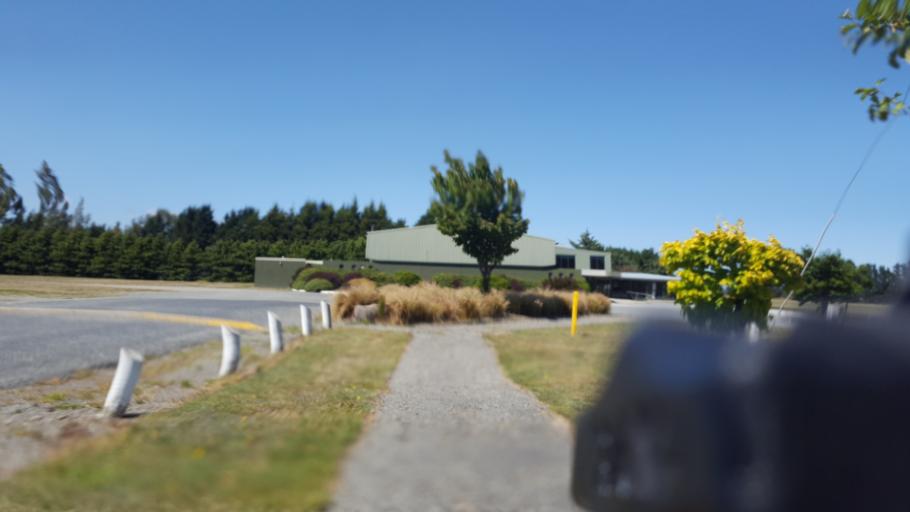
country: NZ
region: Otago
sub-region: Dunedin City
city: Dunedin
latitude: -45.1317
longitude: 170.1059
